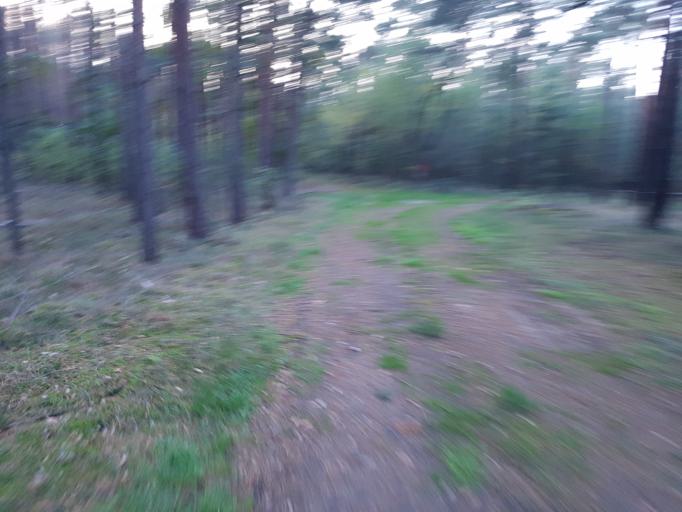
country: DE
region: Brandenburg
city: Bad Liebenwerda
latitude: 51.5424
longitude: 13.3832
